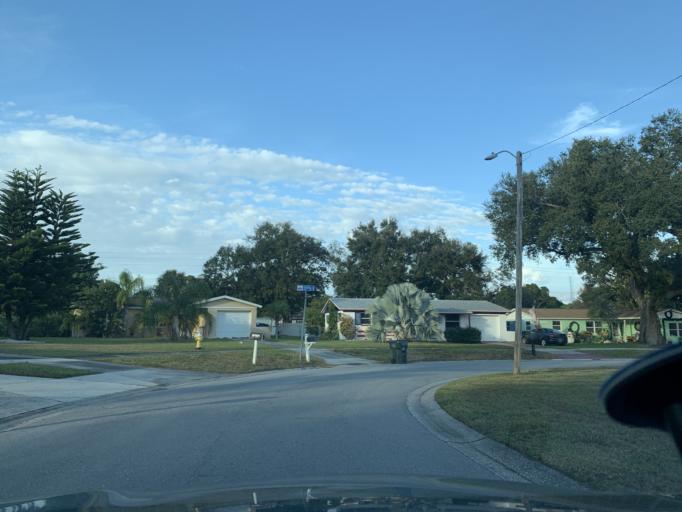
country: US
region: Florida
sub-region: Pinellas County
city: Ridgecrest
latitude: 27.8865
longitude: -82.7967
